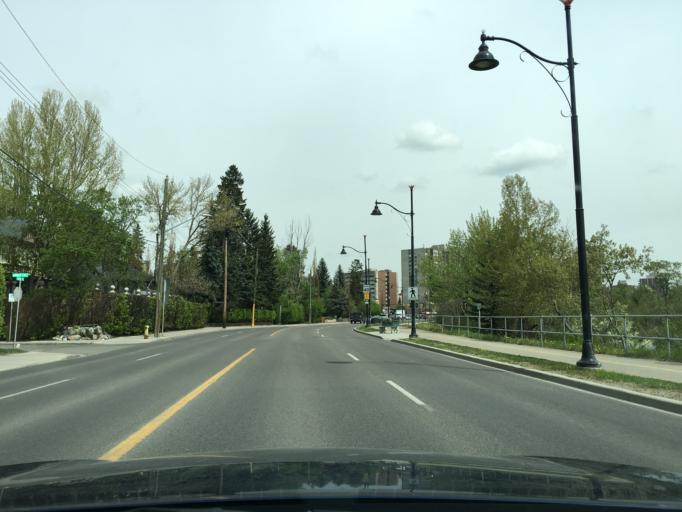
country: CA
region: Alberta
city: Calgary
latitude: 51.0285
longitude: -114.0763
